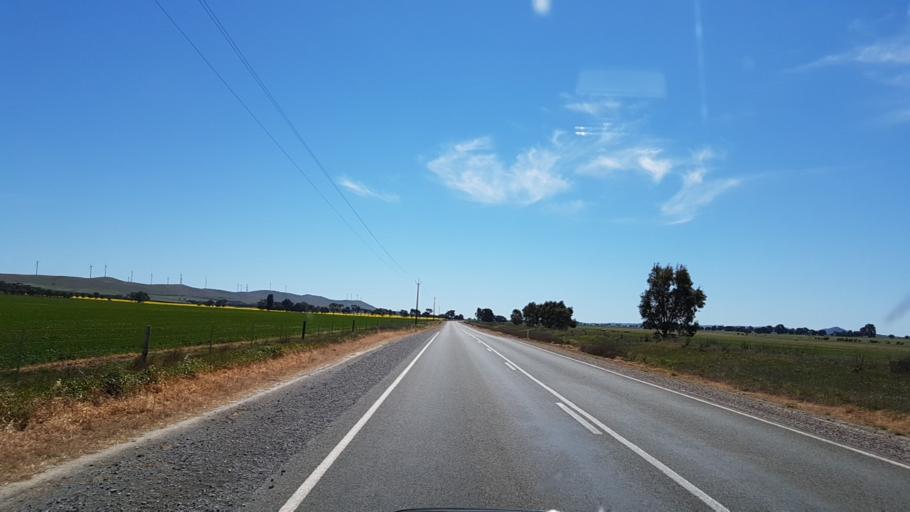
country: AU
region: South Australia
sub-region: Clare and Gilbert Valleys
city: Clare
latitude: -33.6033
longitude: 138.8918
